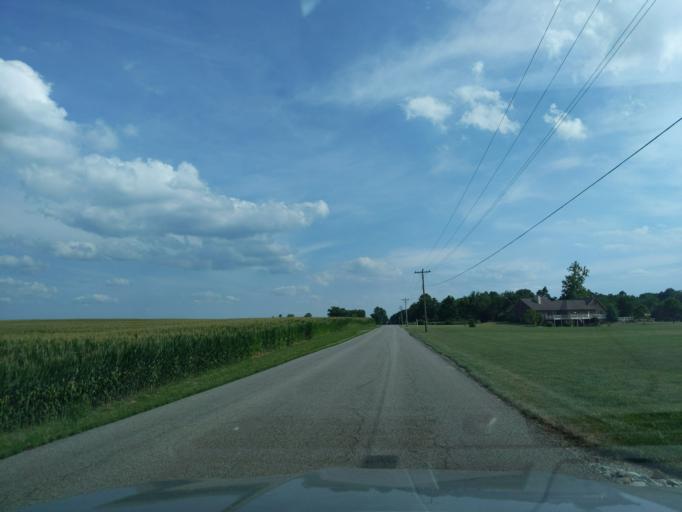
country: US
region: Indiana
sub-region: Decatur County
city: Greensburg
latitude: 39.3170
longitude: -85.4703
